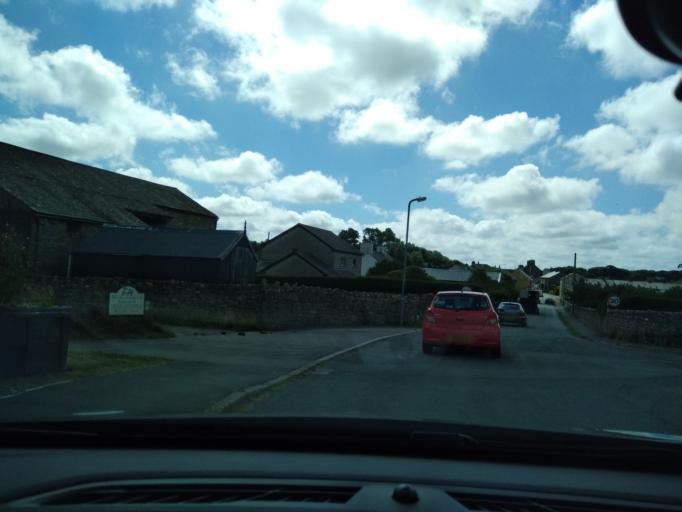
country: GB
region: England
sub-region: Cumbria
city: Millom
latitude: 54.2277
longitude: -3.3316
